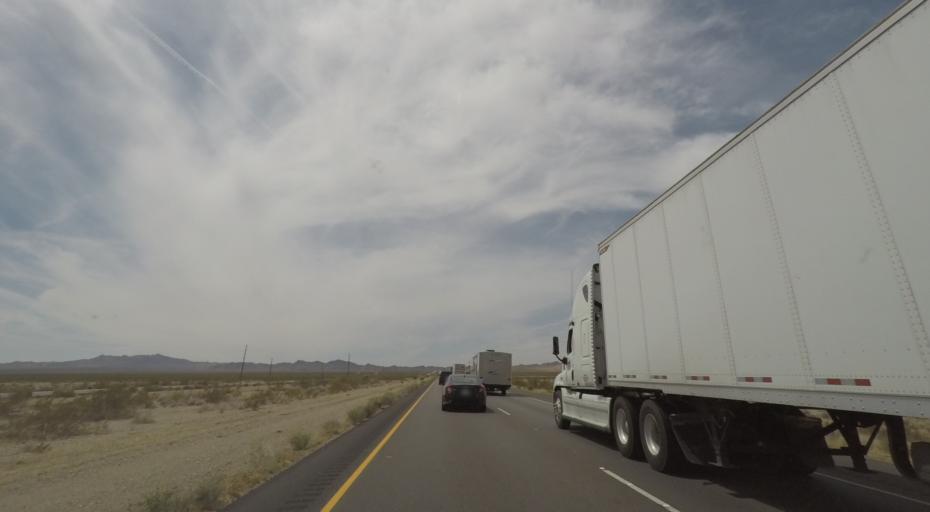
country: US
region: California
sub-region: San Bernardino County
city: Needles
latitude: 34.8449
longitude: -114.9716
